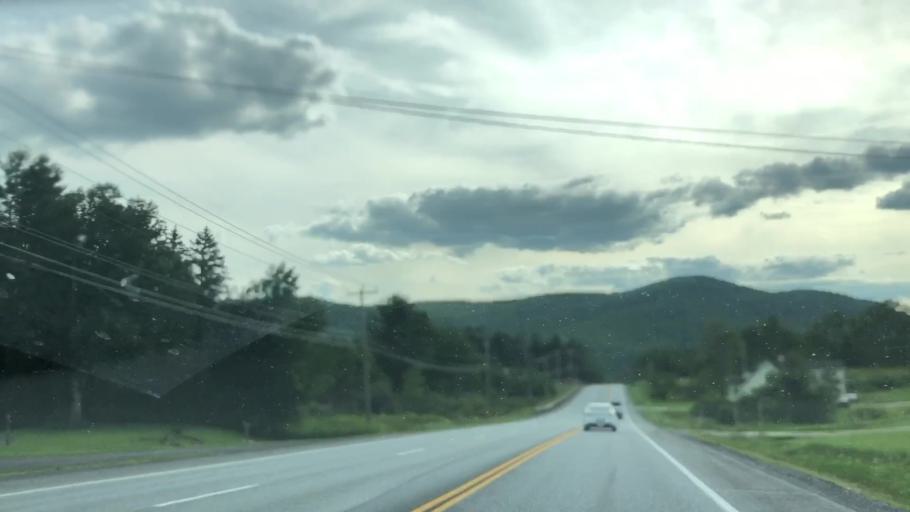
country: US
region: Vermont
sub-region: Rutland County
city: Rutland
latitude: 43.6536
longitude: -72.8892
